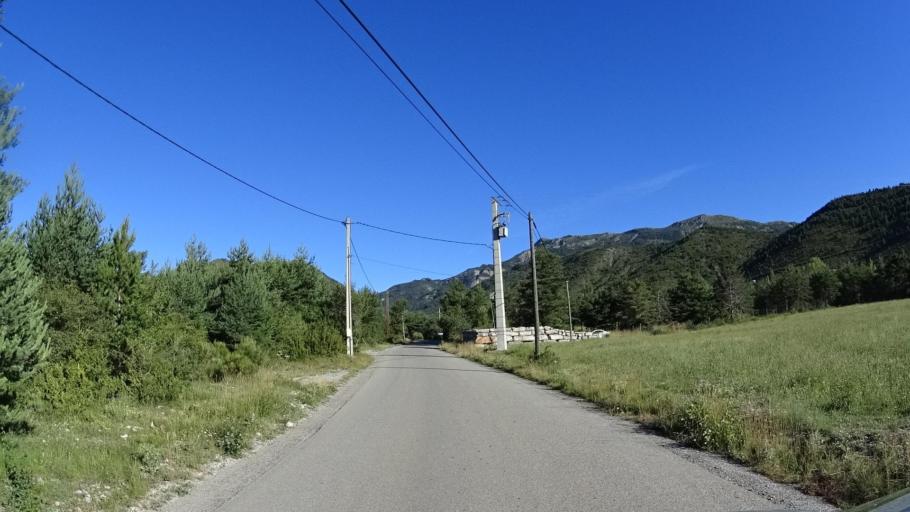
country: FR
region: Provence-Alpes-Cote d'Azur
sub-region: Departement des Alpes-de-Haute-Provence
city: Castellane
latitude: 43.8743
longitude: 6.5097
